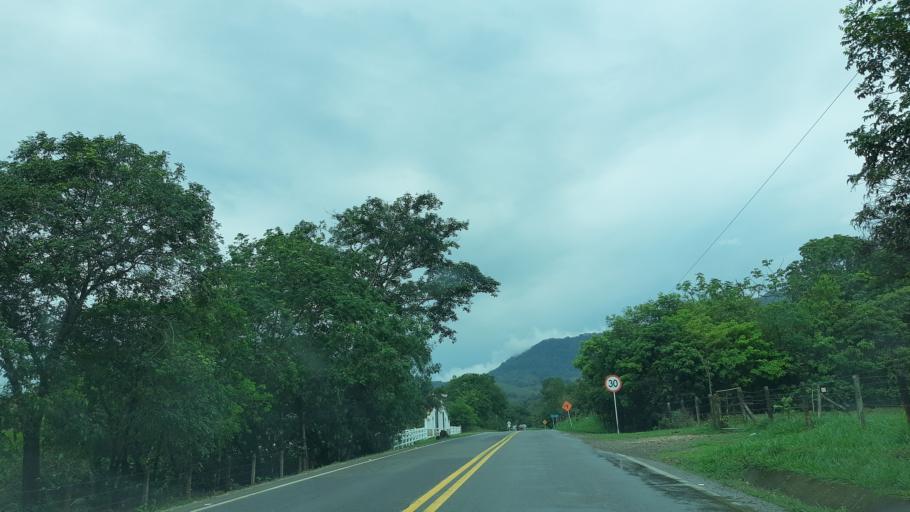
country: CO
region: Casanare
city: Monterrey
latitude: 4.8418
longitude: -72.9508
